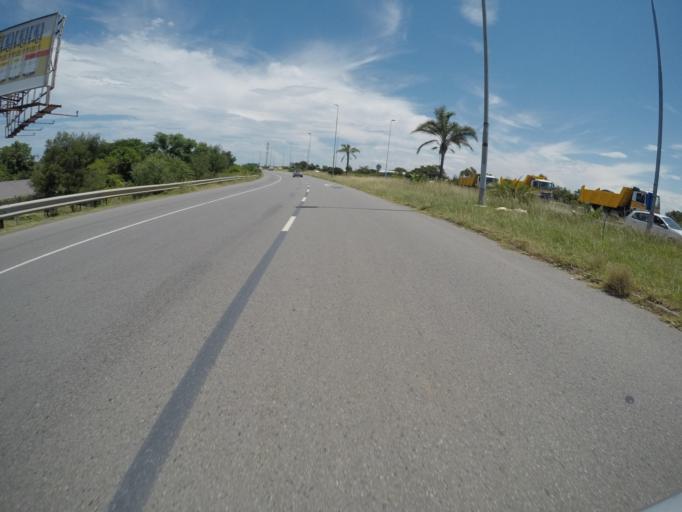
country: ZA
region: Eastern Cape
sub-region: Buffalo City Metropolitan Municipality
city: East London
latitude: -33.0368
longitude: 27.8343
